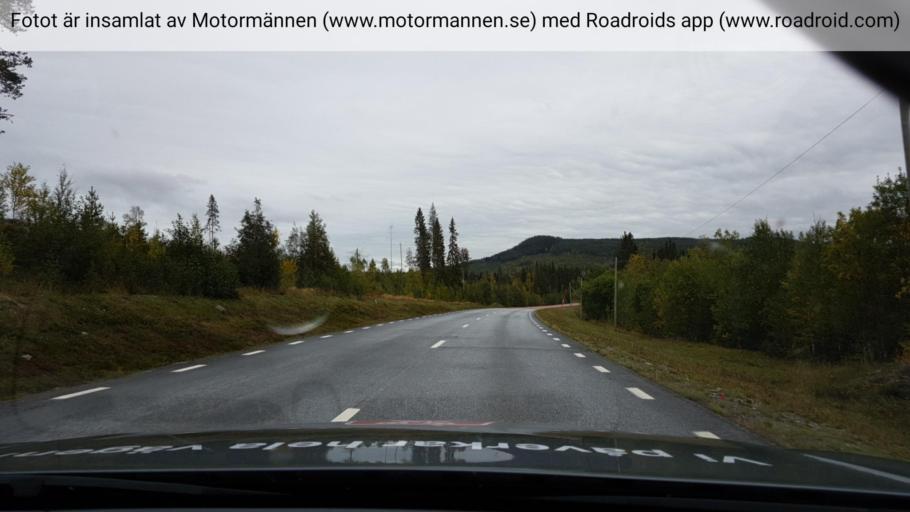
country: SE
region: Vaesterbotten
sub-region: Dorotea Kommun
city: Dorotea
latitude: 64.1934
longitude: 16.3001
